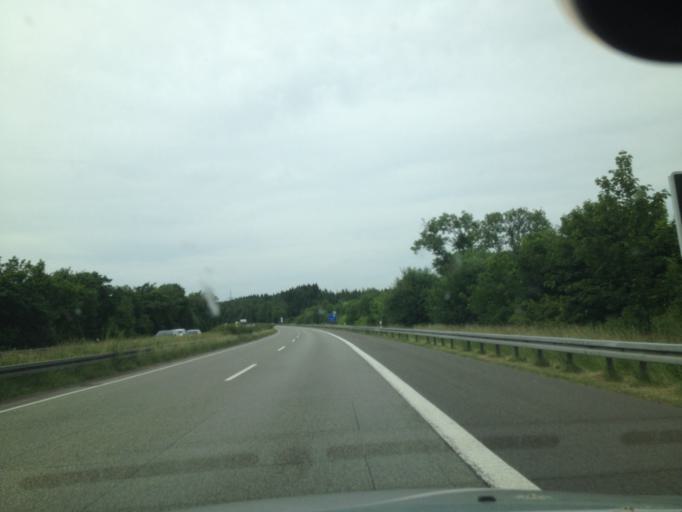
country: DE
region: North Rhine-Westphalia
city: Meinerzhagen
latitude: 51.1447
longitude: 7.6756
